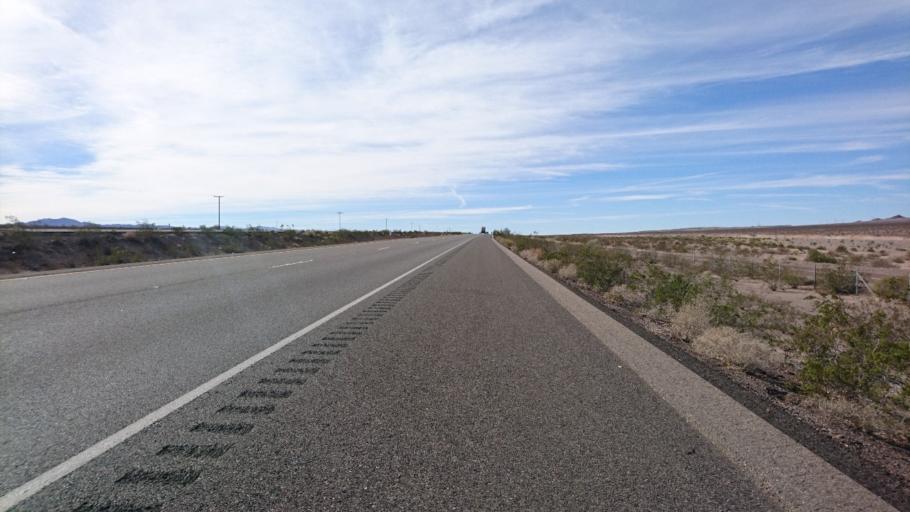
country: US
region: California
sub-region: San Bernardino County
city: Joshua Tree
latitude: 34.7268
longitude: -116.2436
